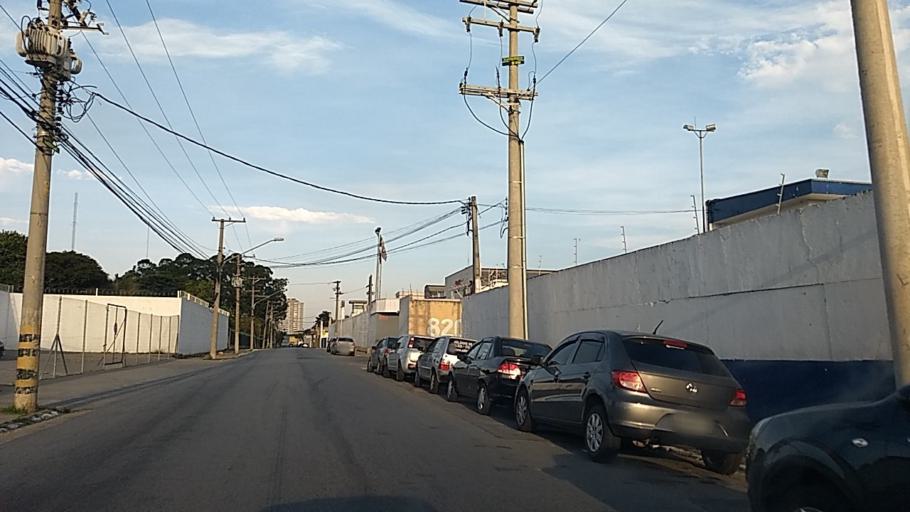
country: BR
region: Sao Paulo
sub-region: Sao Paulo
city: Sao Paulo
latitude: -23.5144
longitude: -46.5997
